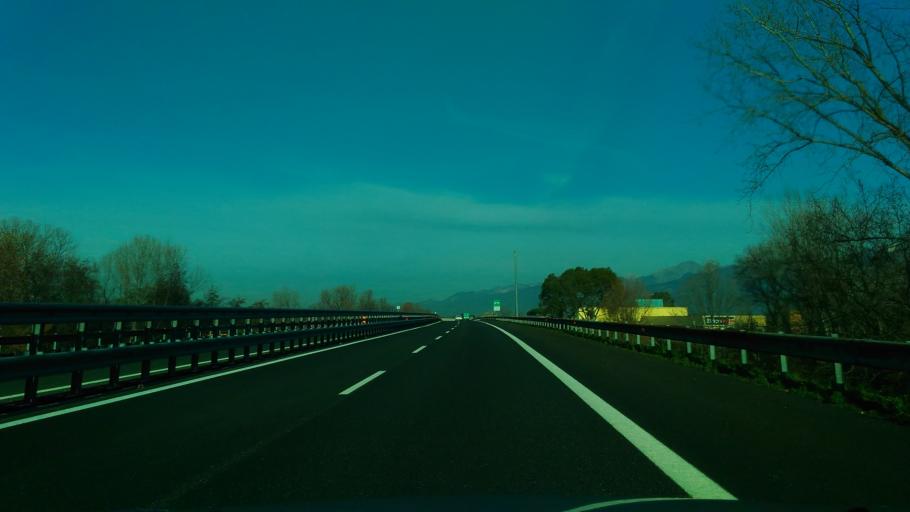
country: IT
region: Tuscany
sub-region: Provincia di Lucca
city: Viareggio
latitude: 43.8700
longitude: 10.2756
